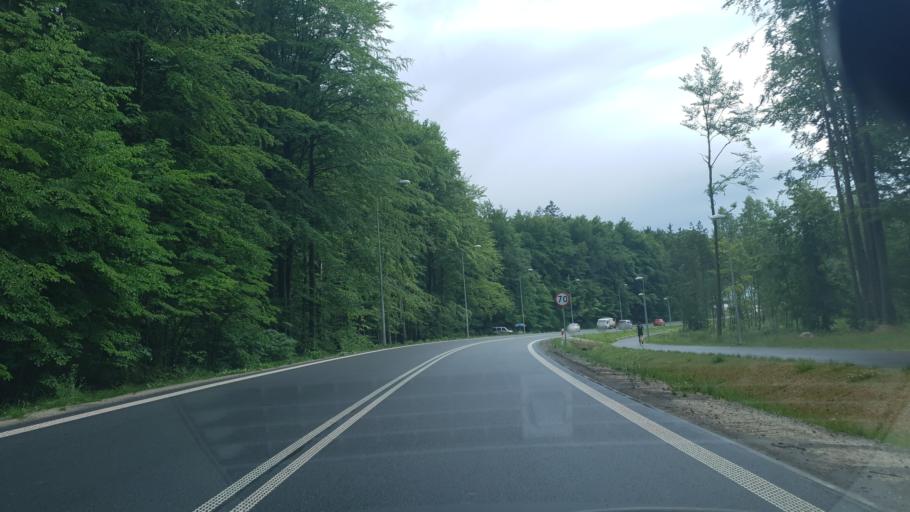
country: PL
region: Pomeranian Voivodeship
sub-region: Powiat kartuski
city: Kartuzy
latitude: 54.3418
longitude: 18.2137
